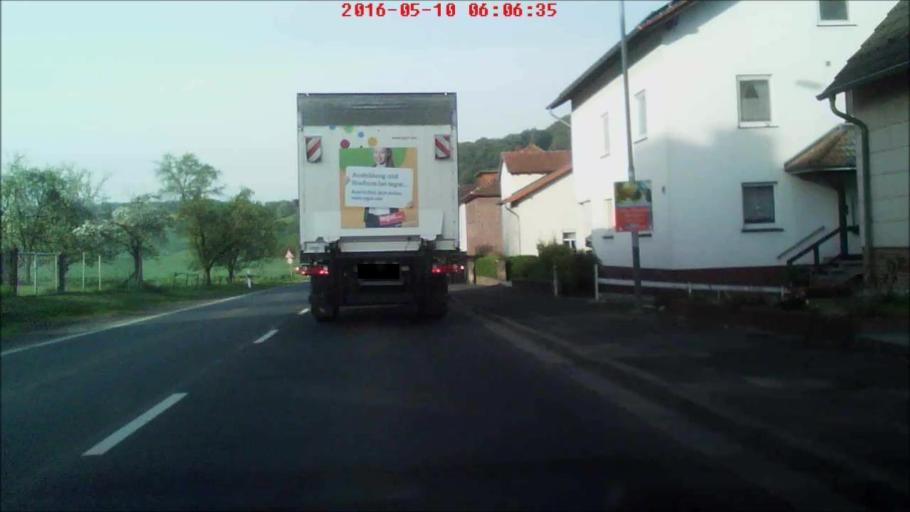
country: DE
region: Hesse
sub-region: Regierungsbezirk Kassel
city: Bad Hersfeld
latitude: 50.8162
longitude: 9.7339
